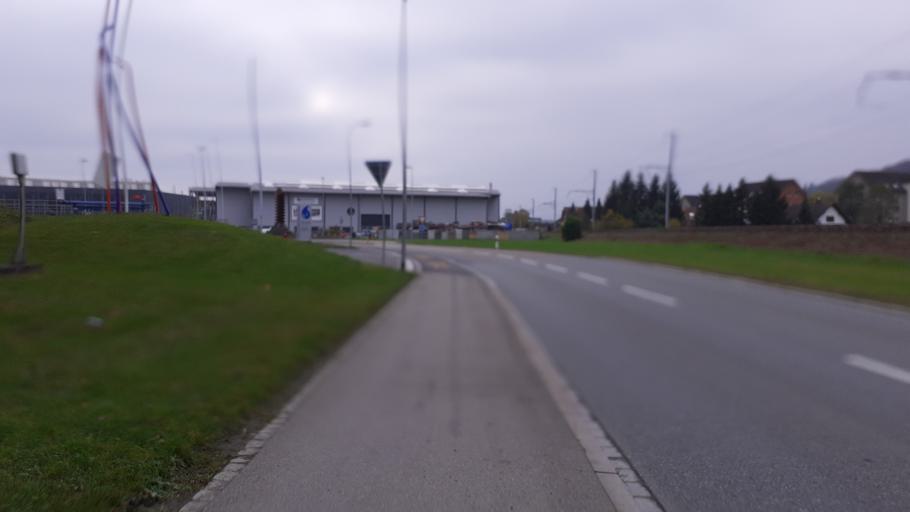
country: CH
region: Saint Gallen
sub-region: Wahlkreis Rheintal
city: Au
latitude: 47.4217
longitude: 9.6374
